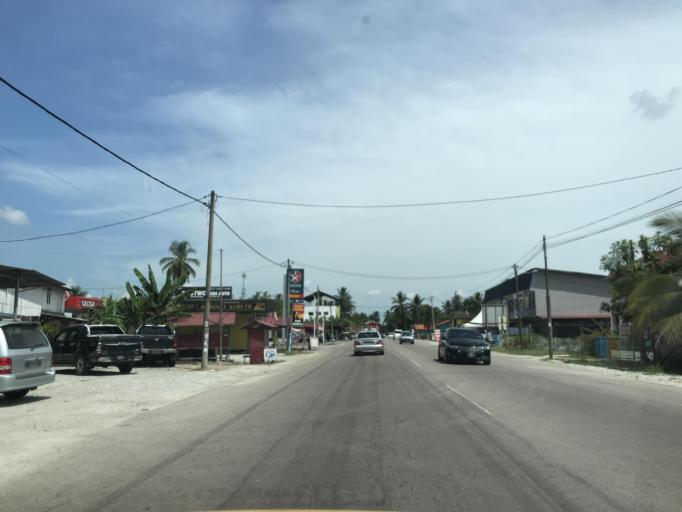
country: MY
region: Kelantan
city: Kota Bharu
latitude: 6.1191
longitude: 102.1912
